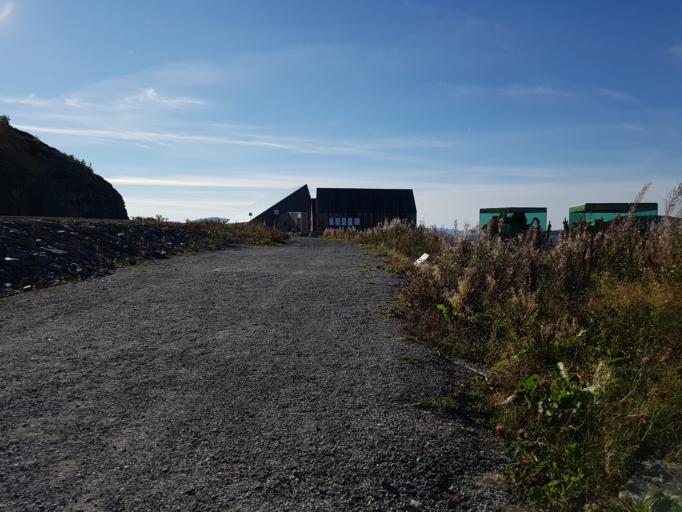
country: NO
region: Sor-Trondelag
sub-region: Afjord
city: A i Afjord
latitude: 64.0475
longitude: 9.9455
